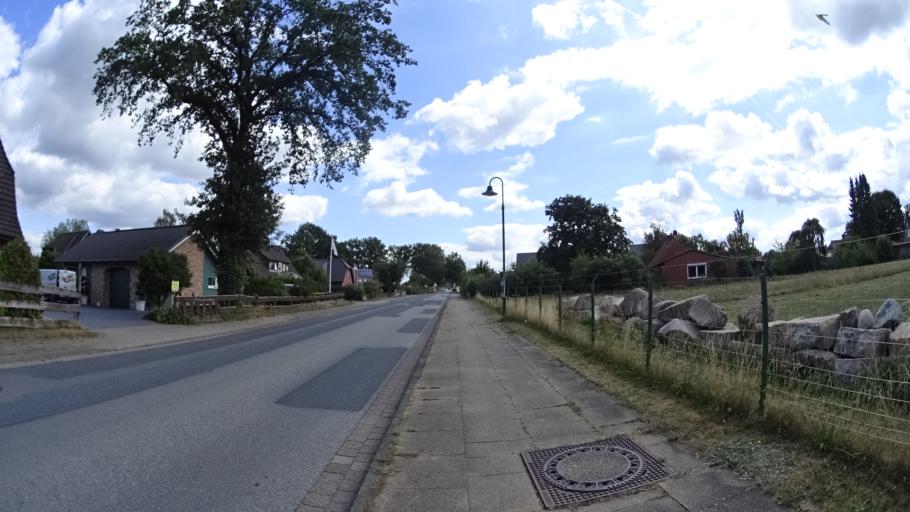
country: DE
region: Lower Saxony
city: Undeloh
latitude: 53.2269
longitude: 9.9213
